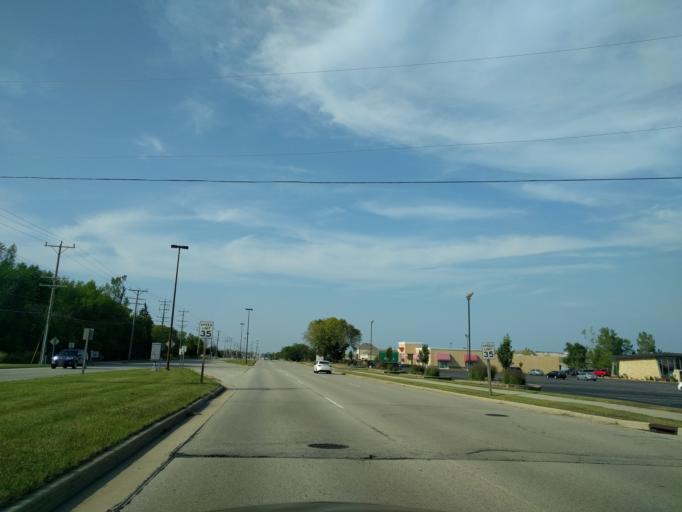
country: US
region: Wisconsin
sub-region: Milwaukee County
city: River Hills
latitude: 43.2143
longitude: -87.9241
